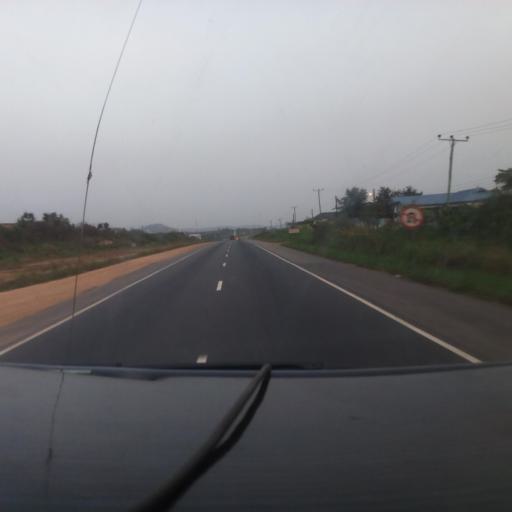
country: GH
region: Eastern
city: Nsawam
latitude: 5.8703
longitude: -0.3677
